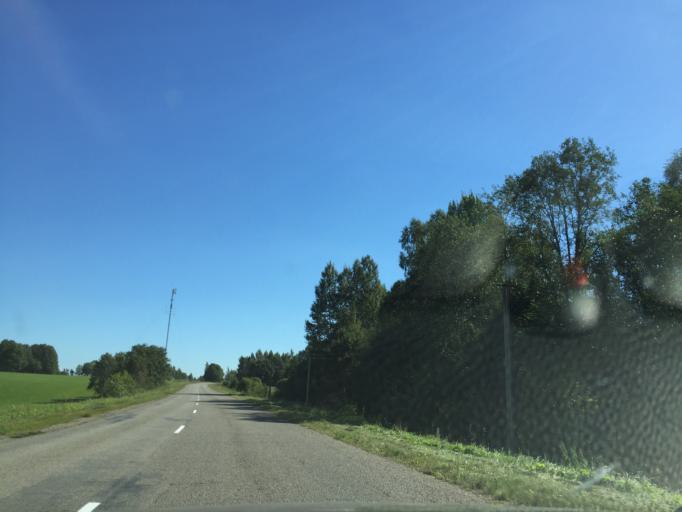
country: LV
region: Akniste
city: Akniste
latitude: 56.0554
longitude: 25.9017
